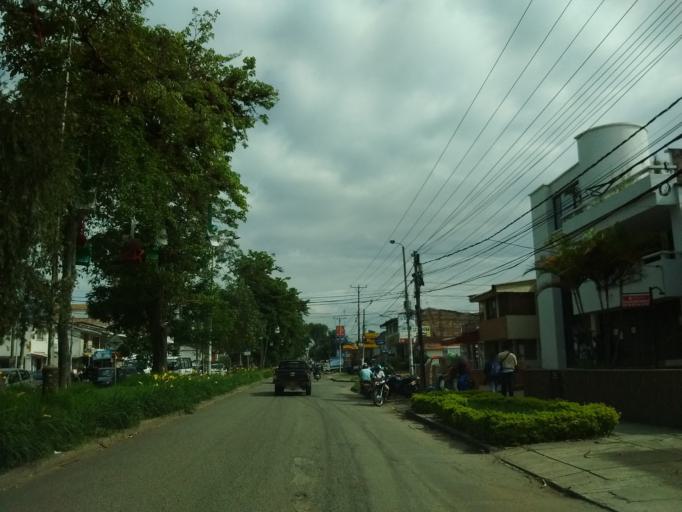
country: CO
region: Cauca
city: Popayan
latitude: 2.4463
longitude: -76.6071
